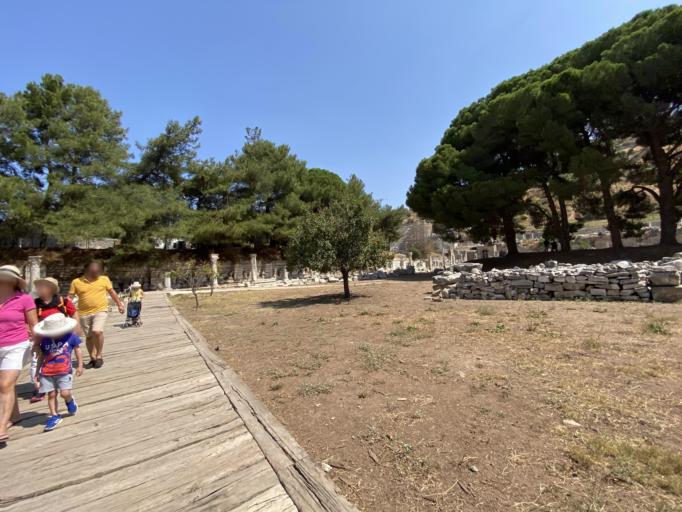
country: TR
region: Izmir
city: Selcuk
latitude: 37.9404
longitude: 27.3403
